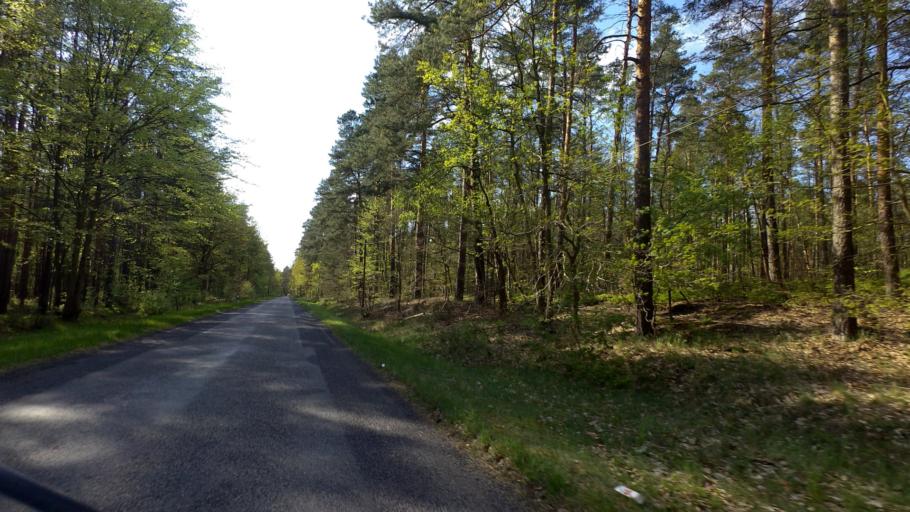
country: DE
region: Brandenburg
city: Zehdenick
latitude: 53.0172
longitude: 13.3990
